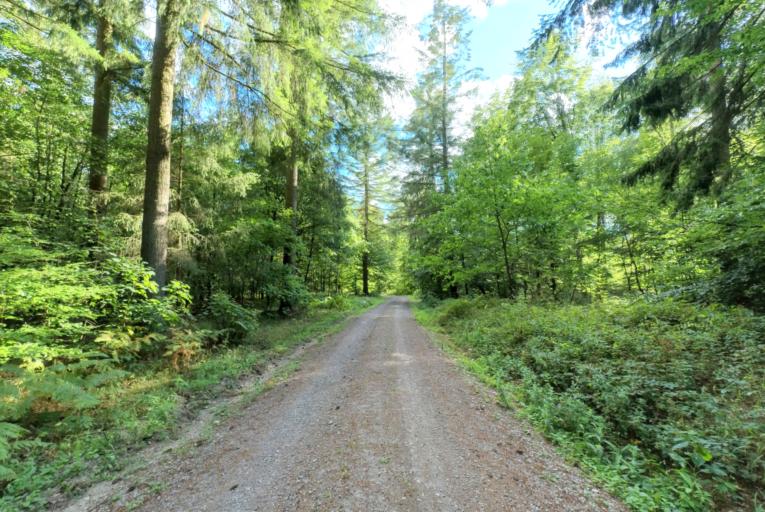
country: DE
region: Baden-Wuerttemberg
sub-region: Karlsruhe Region
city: Fahrenbach
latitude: 49.4125
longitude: 9.1133
